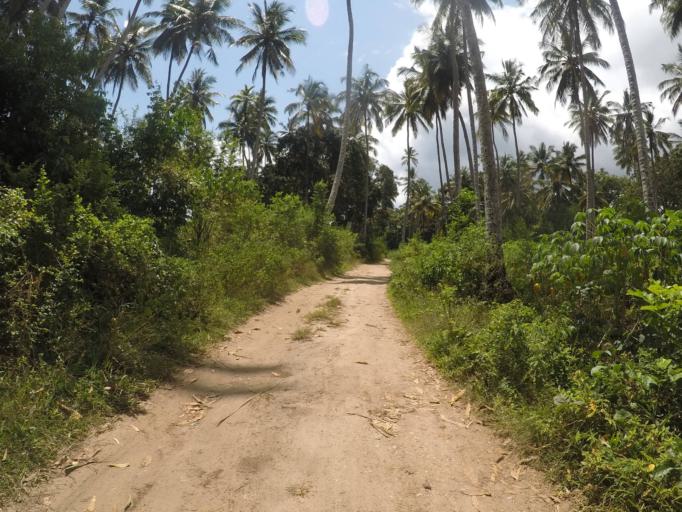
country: TZ
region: Zanzibar North
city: Mkokotoni
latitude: -5.9906
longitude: 39.1869
